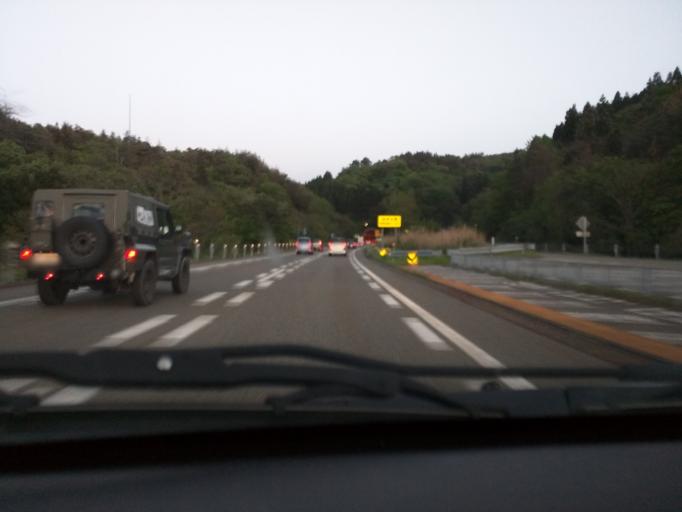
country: JP
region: Niigata
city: Kashiwazaki
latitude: 37.3453
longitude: 138.5130
